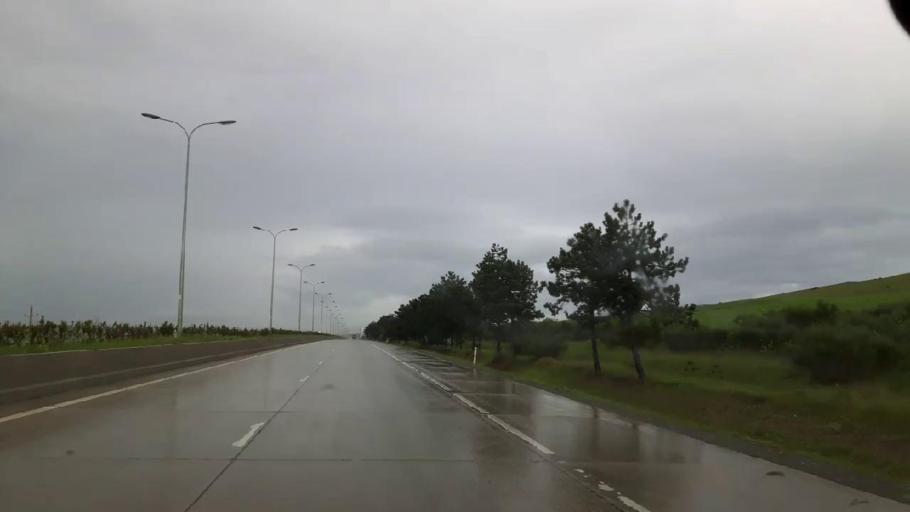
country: GE
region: Shida Kartli
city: Gori
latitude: 42.0183
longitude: 44.0204
